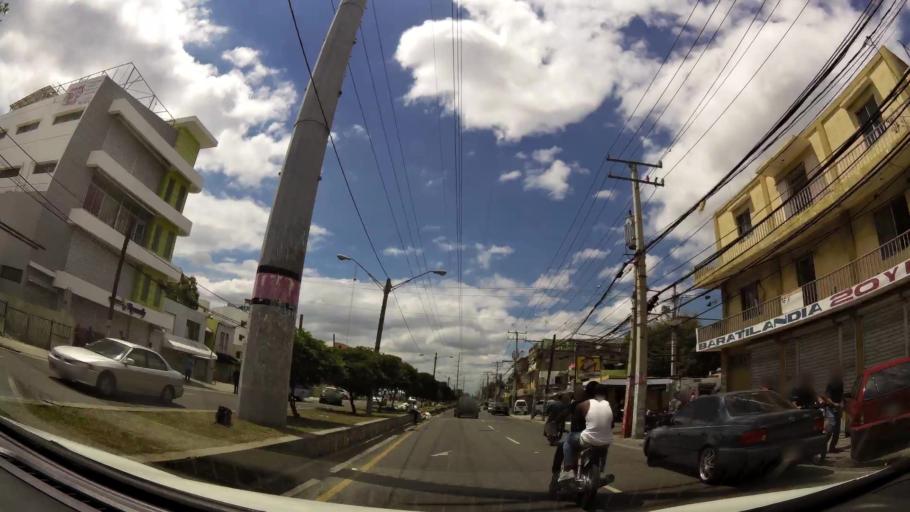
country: DO
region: Nacional
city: Bella Vista
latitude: 18.4332
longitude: -69.9627
